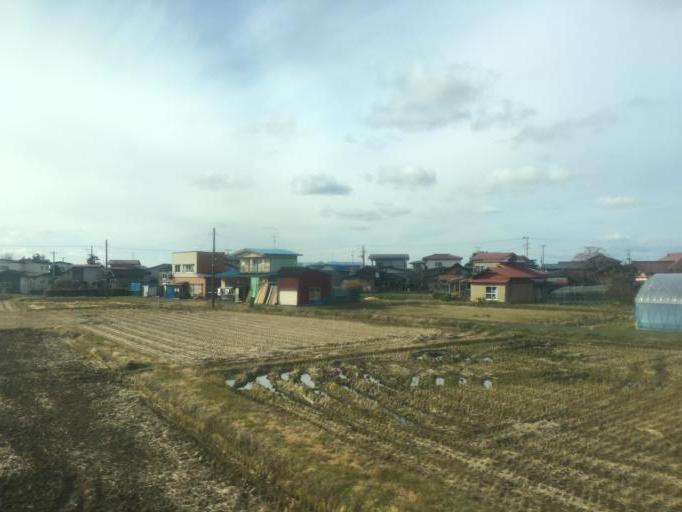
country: JP
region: Akita
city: Tenno
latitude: 39.9580
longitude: 140.0759
